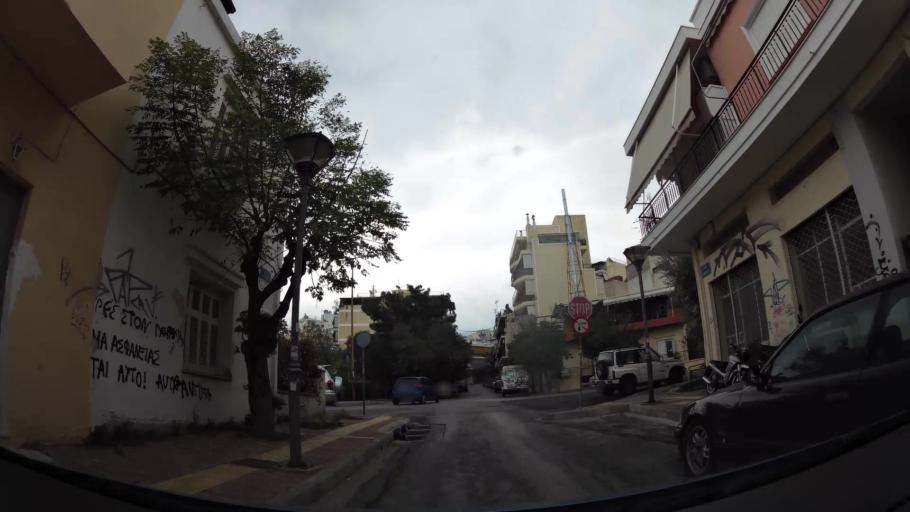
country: GR
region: Attica
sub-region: Nomarchia Athinas
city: Vyronas
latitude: 37.9537
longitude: 23.7608
